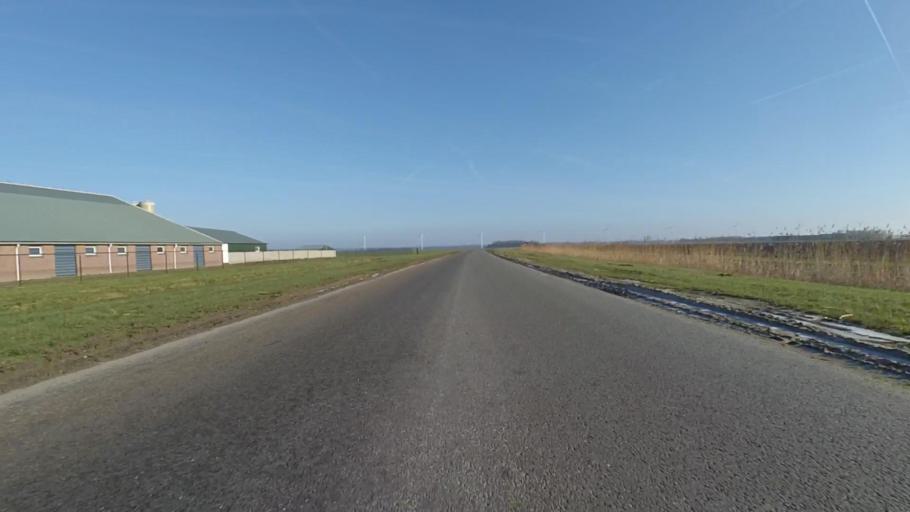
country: NL
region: Utrecht
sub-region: Gemeente Bunschoten
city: Spakenburg
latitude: 52.3032
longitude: 5.4024
